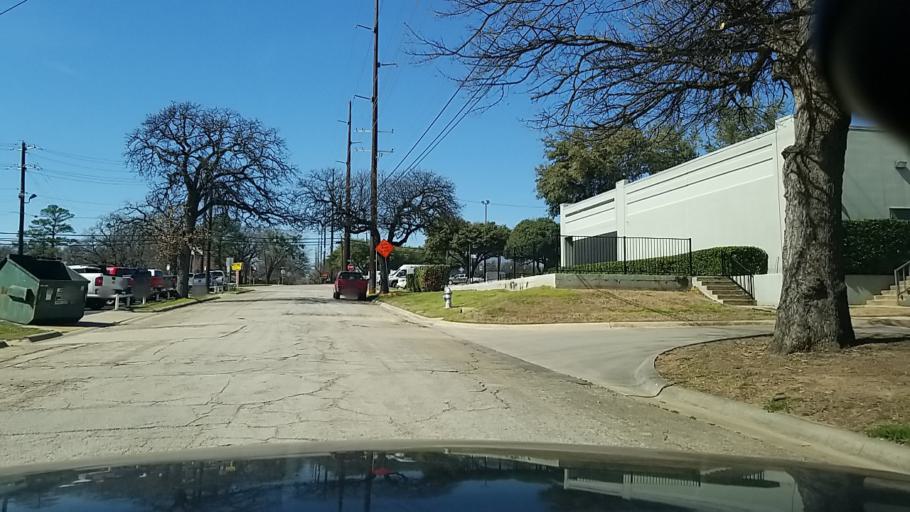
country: US
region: Texas
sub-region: Denton County
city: Denton
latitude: 33.2021
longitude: -97.1264
